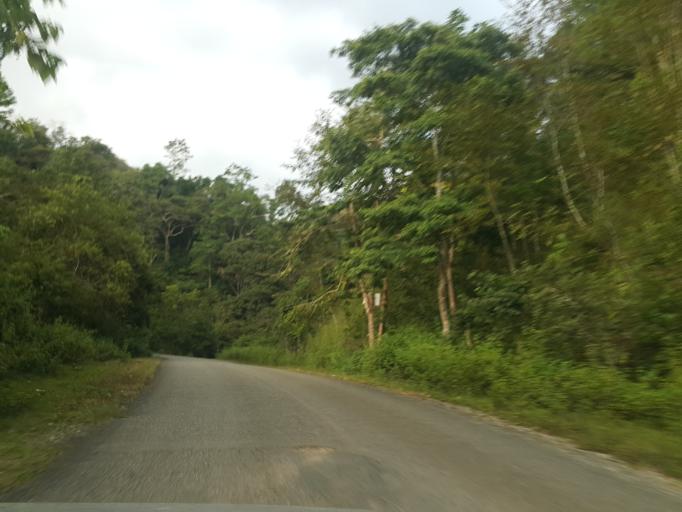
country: TH
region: Mae Hong Son
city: Khun Yuam
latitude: 18.7640
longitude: 98.1859
